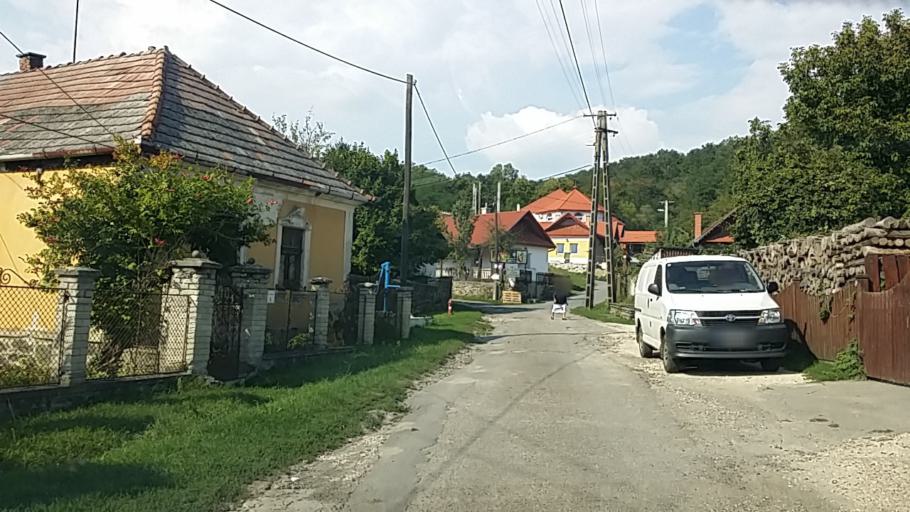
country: HU
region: Nograd
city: Bujak
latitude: 47.8664
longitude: 19.5021
